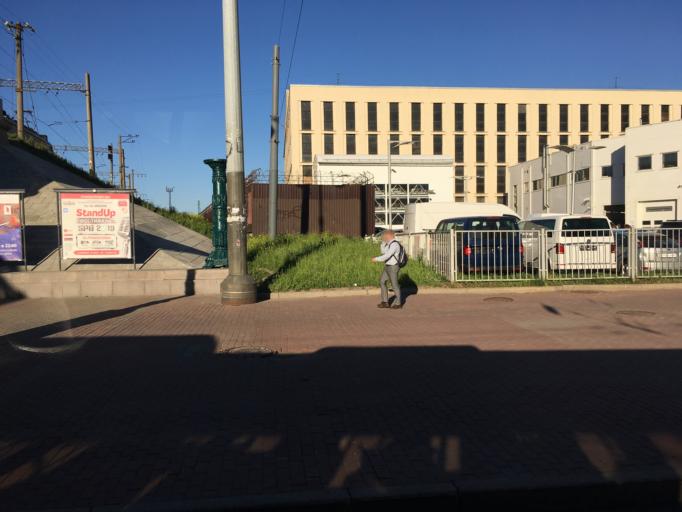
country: RU
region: St.-Petersburg
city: Admiralteisky
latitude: 59.8828
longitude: 30.3204
